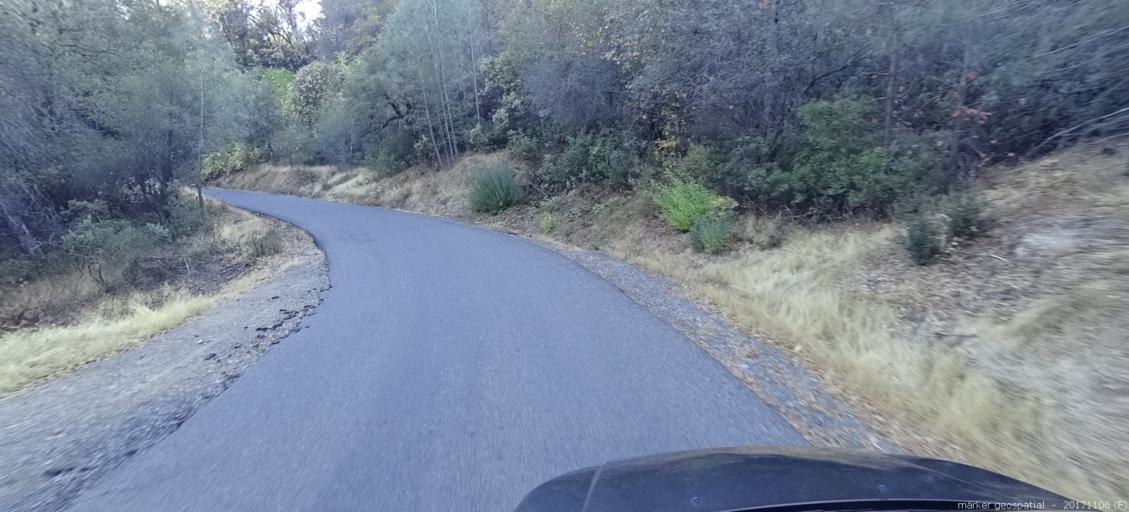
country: US
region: California
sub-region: Shasta County
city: Shasta
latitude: 40.6036
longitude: -122.4911
